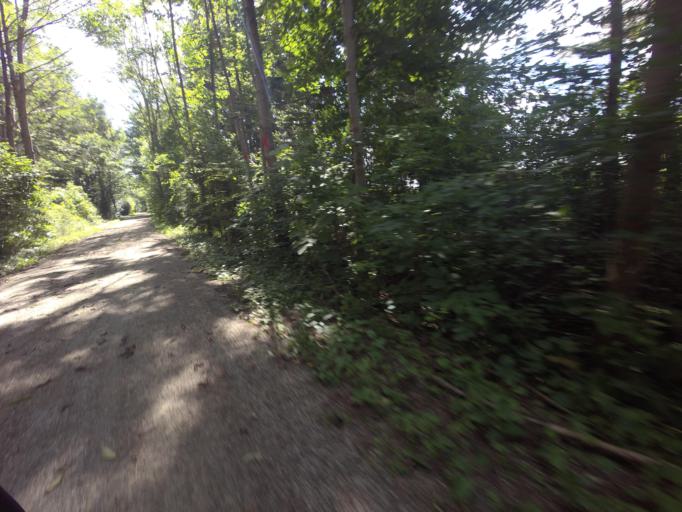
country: CA
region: Ontario
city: Huron East
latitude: 43.6780
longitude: -81.2939
